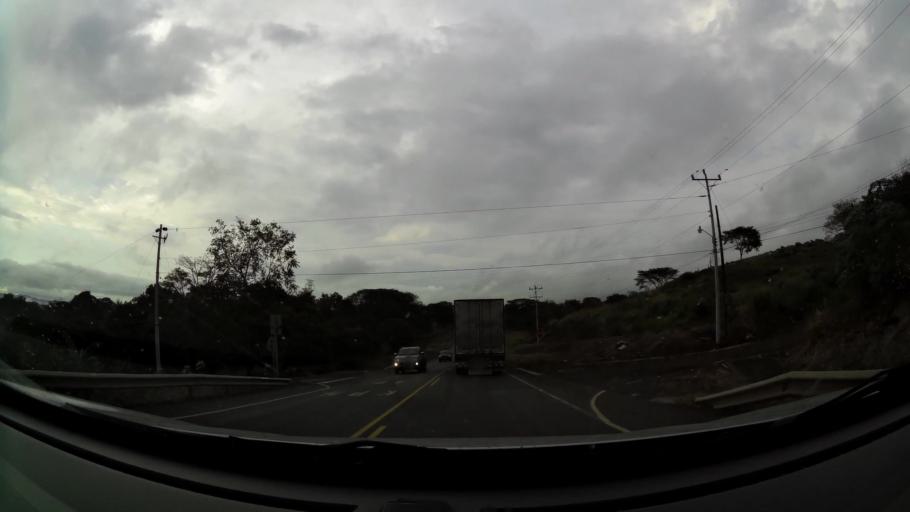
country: CR
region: Alajuela
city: Carrillos
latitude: 9.9673
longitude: -84.2802
